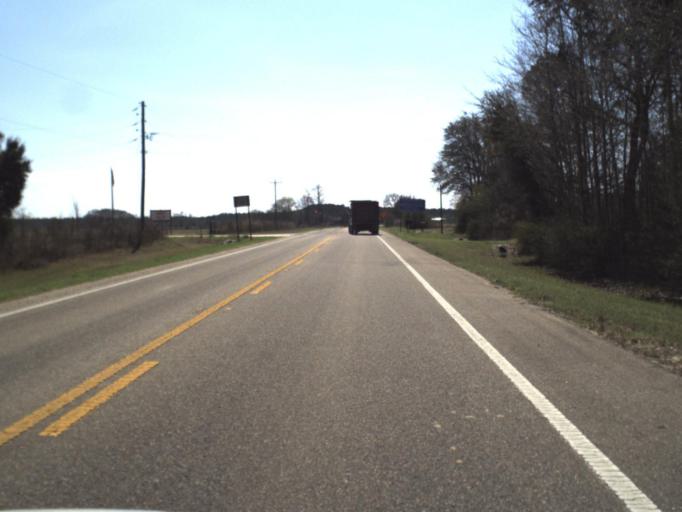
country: US
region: Florida
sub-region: Calhoun County
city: Blountstown
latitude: 30.5156
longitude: -85.0322
